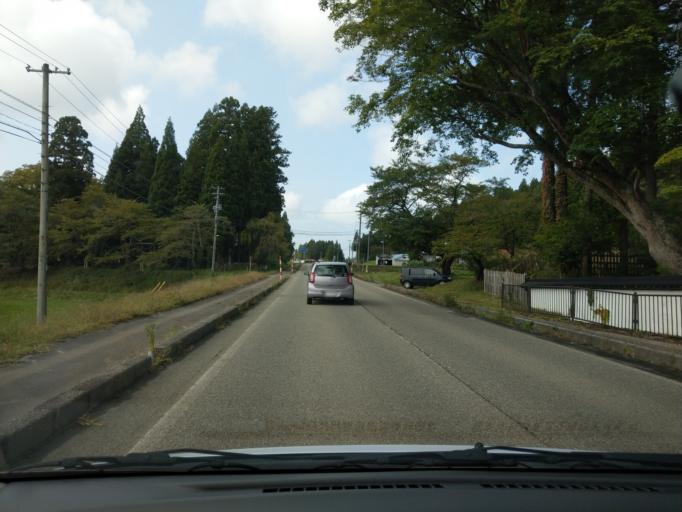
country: JP
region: Akita
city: Omagari
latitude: 39.4412
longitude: 140.3508
